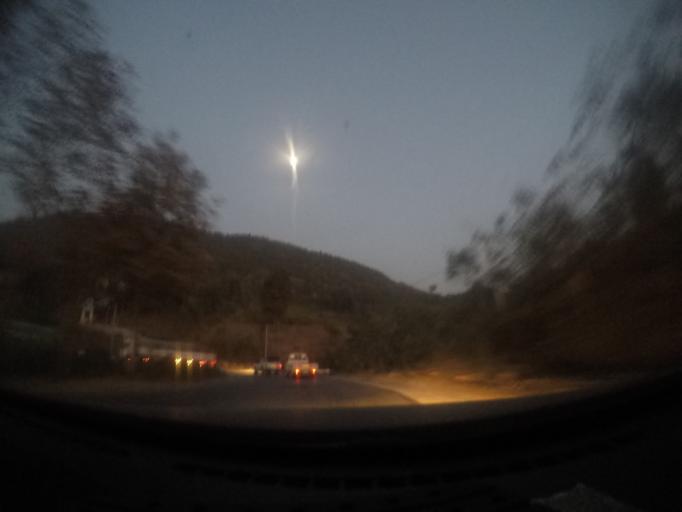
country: MM
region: Mandalay
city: Yamethin
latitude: 20.7043
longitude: 96.5156
